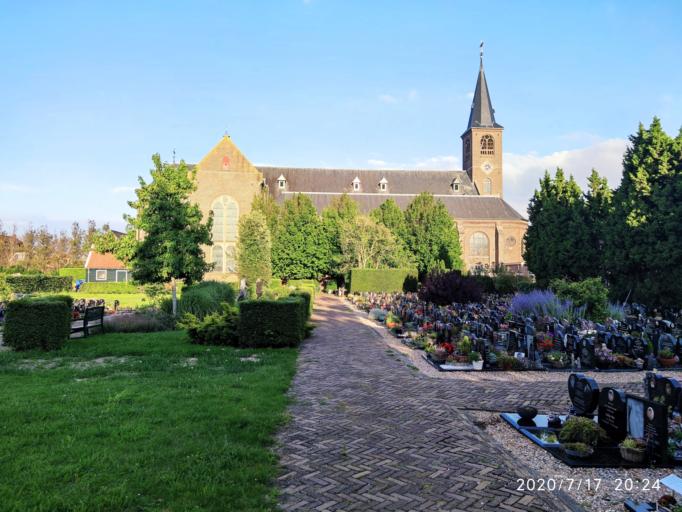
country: NL
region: North Holland
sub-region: Gemeente Edam-Volendam
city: Volendam
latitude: 52.4964
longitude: 5.0763
